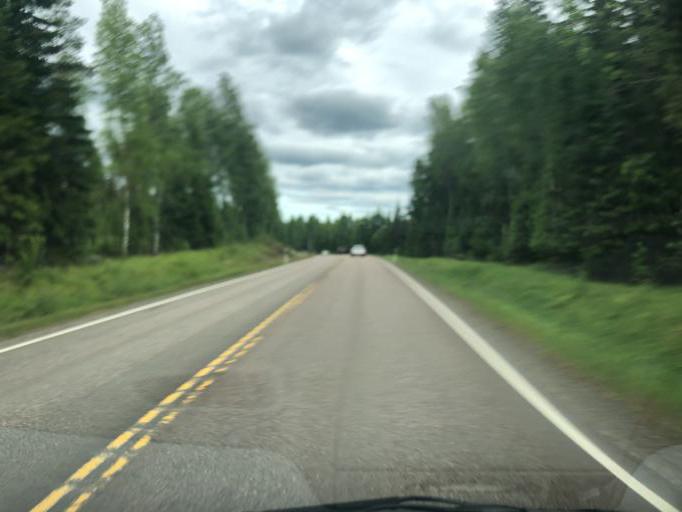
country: FI
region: Kymenlaakso
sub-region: Kouvola
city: Kouvola
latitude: 61.0425
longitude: 27.0073
